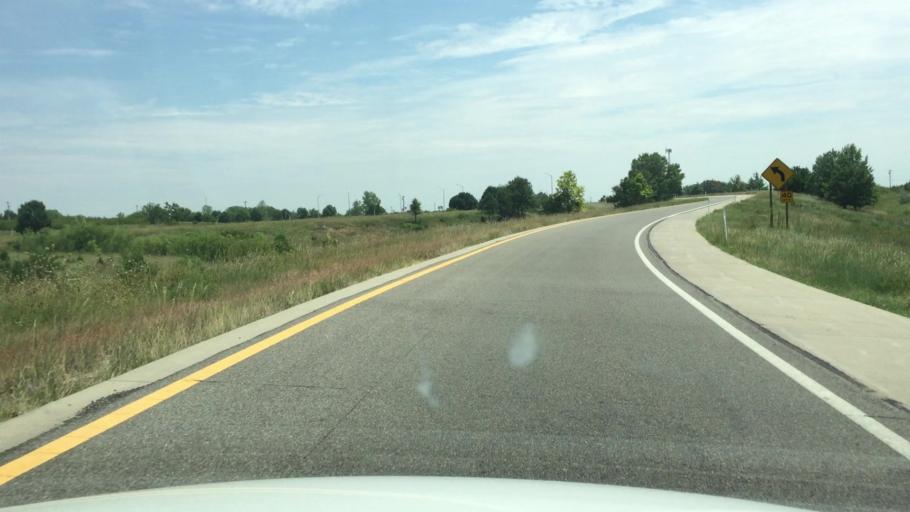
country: US
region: Kansas
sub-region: Shawnee County
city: Topeka
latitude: 39.0336
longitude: -95.6276
